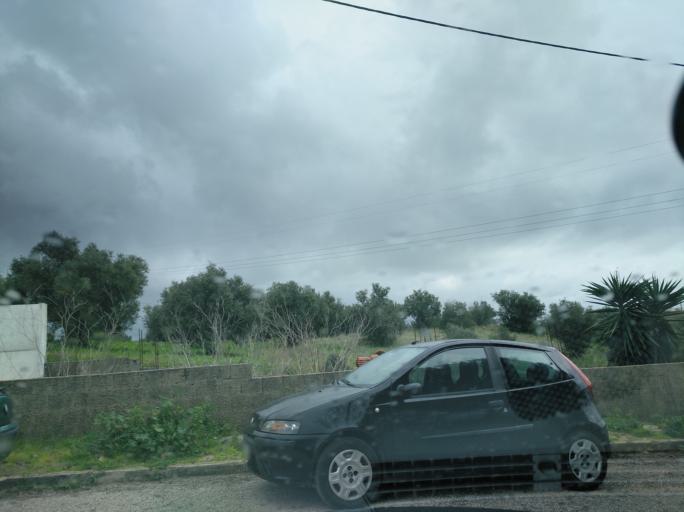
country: PT
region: Lisbon
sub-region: Odivelas
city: Famoes
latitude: 38.7879
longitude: -9.2043
